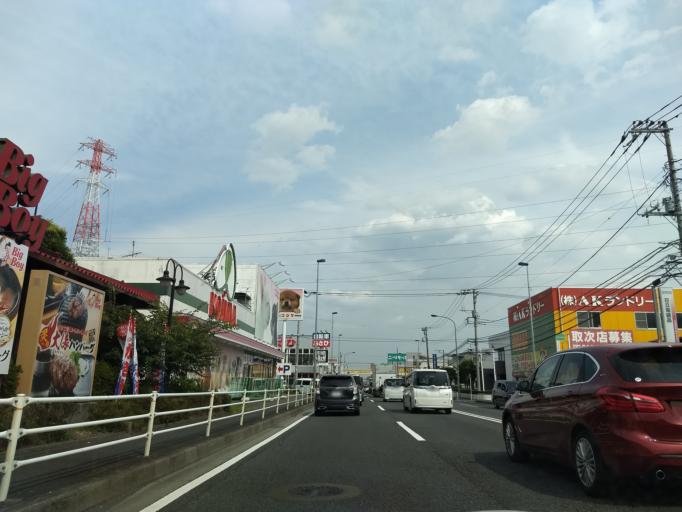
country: JP
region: Tokyo
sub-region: Machida-shi
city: Machida
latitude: 35.5581
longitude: 139.4060
